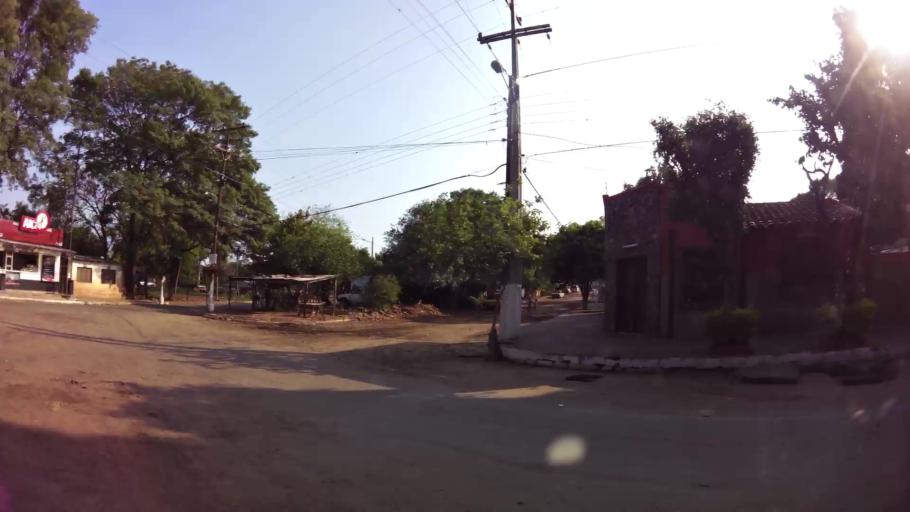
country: PY
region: Central
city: Villa Elisa
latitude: -25.3477
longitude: -57.5849
